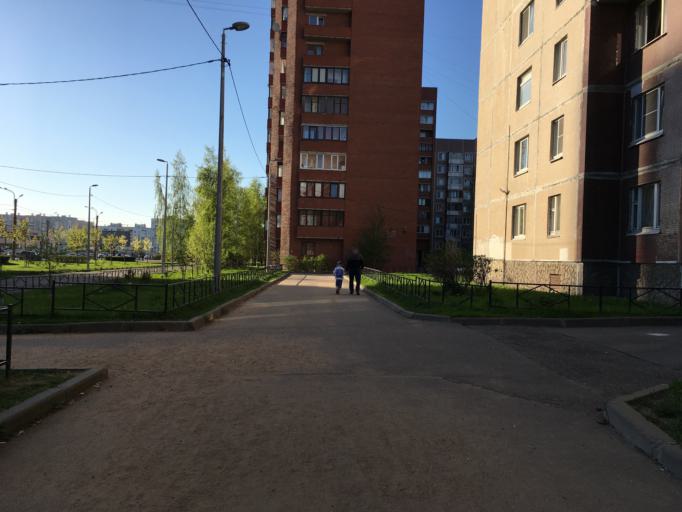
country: RU
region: Leningrad
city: Untolovo
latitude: 60.0243
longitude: 30.2412
